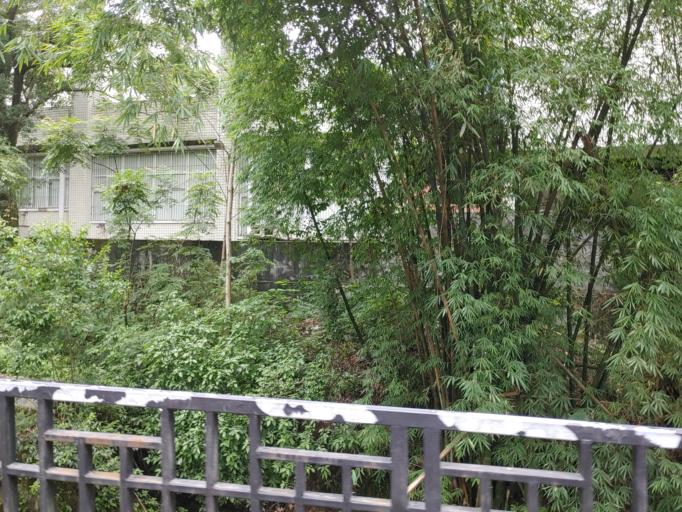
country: CN
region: Chongqing Shi
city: Shuangfeng
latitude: 29.9703
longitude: 106.4154
